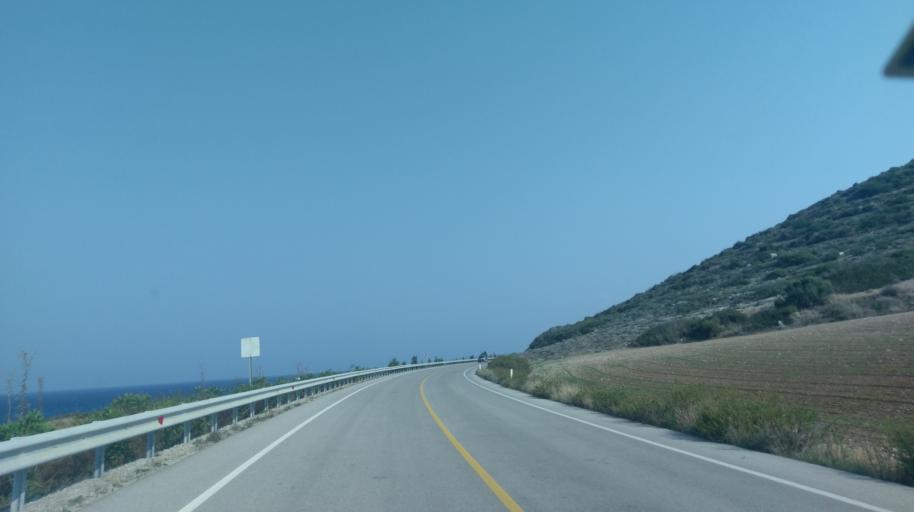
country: CY
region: Ammochostos
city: Leonarisso
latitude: 35.4906
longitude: 34.0813
